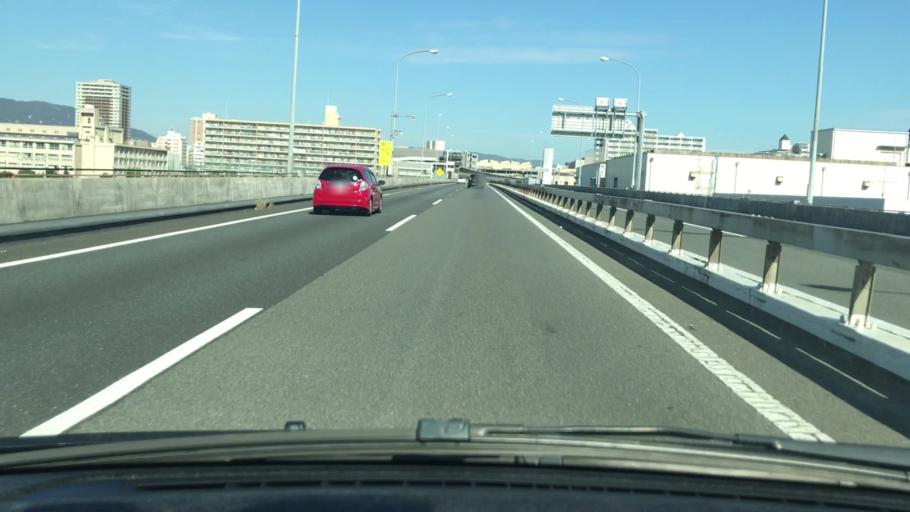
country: JP
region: Hyogo
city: Nishinomiya-hama
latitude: 34.7367
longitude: 135.3595
